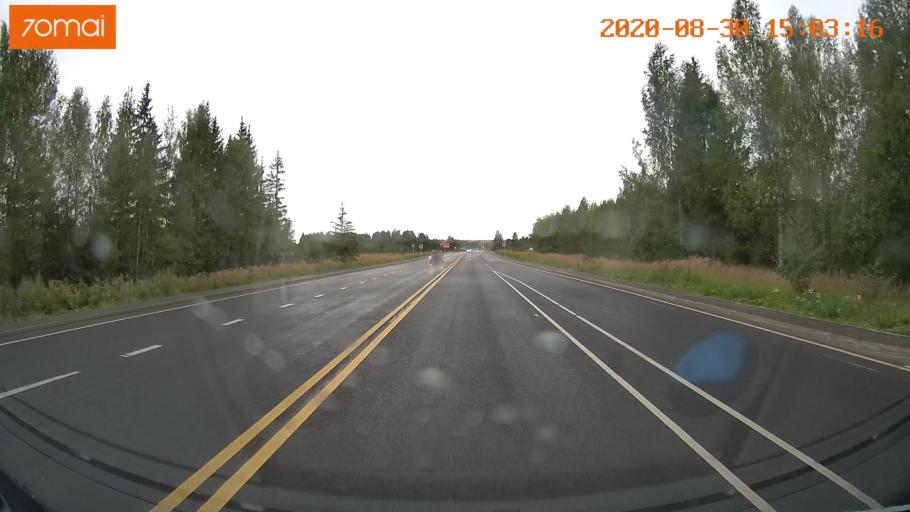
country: RU
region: Ivanovo
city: Staraya Vichuga
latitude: 57.3012
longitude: 41.9144
